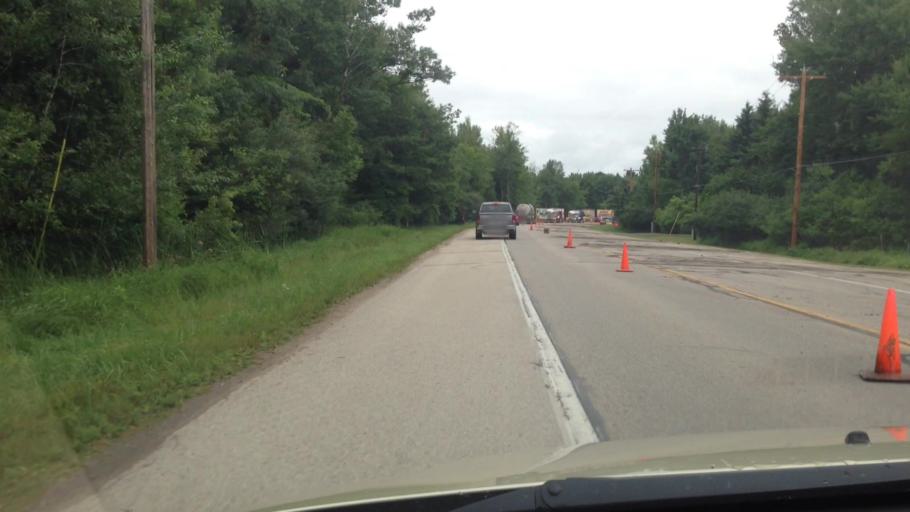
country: US
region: Michigan
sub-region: Delta County
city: Escanaba
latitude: 45.7027
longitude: -87.1011
